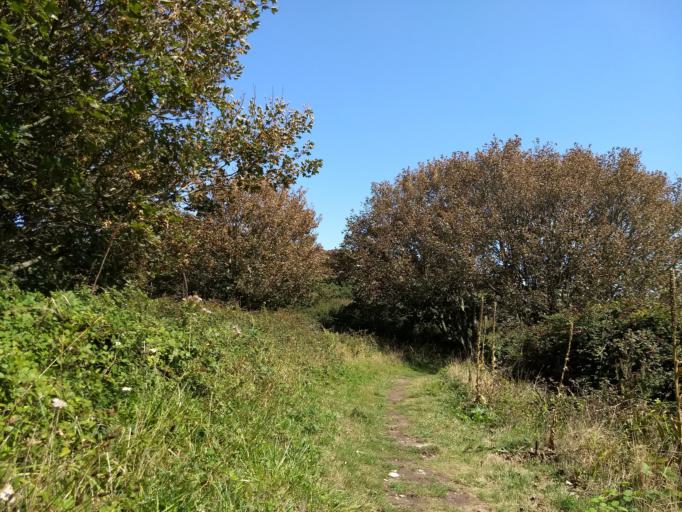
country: GB
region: England
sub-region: Isle of Wight
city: Totland
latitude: 50.6709
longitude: -1.5657
